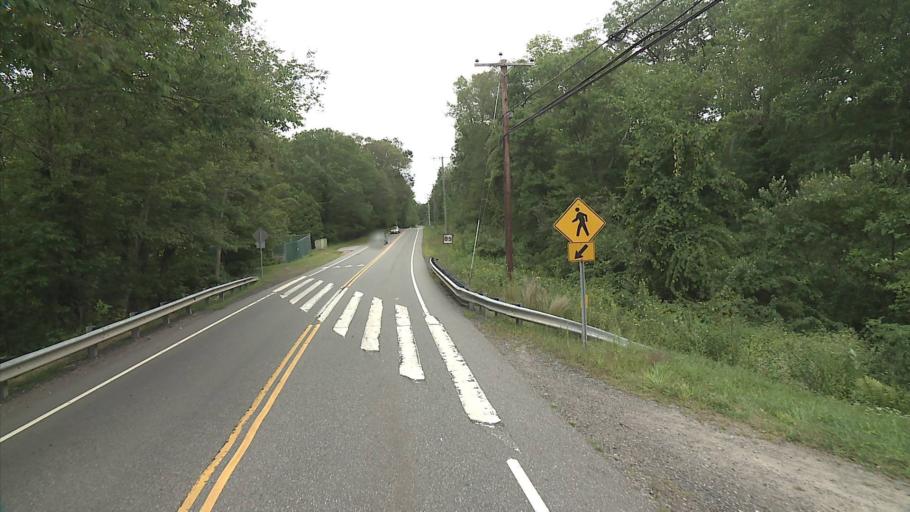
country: US
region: Connecticut
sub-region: Tolland County
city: Hebron
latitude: 41.6194
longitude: -72.3442
